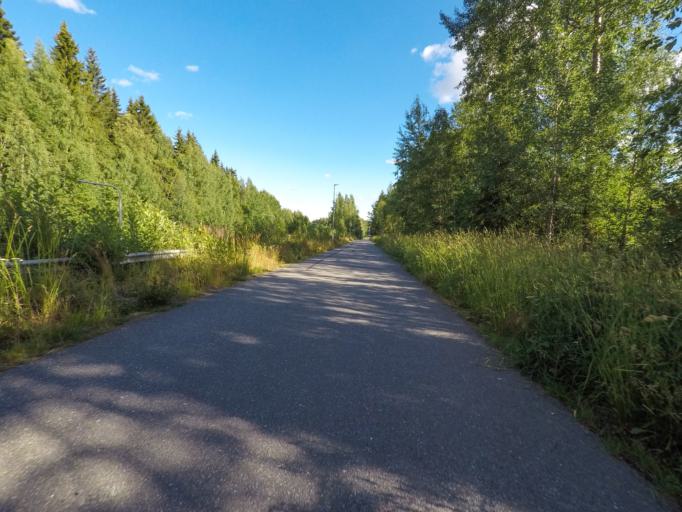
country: FI
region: South Karelia
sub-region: Lappeenranta
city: Lappeenranta
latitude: 61.0907
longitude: 28.1413
